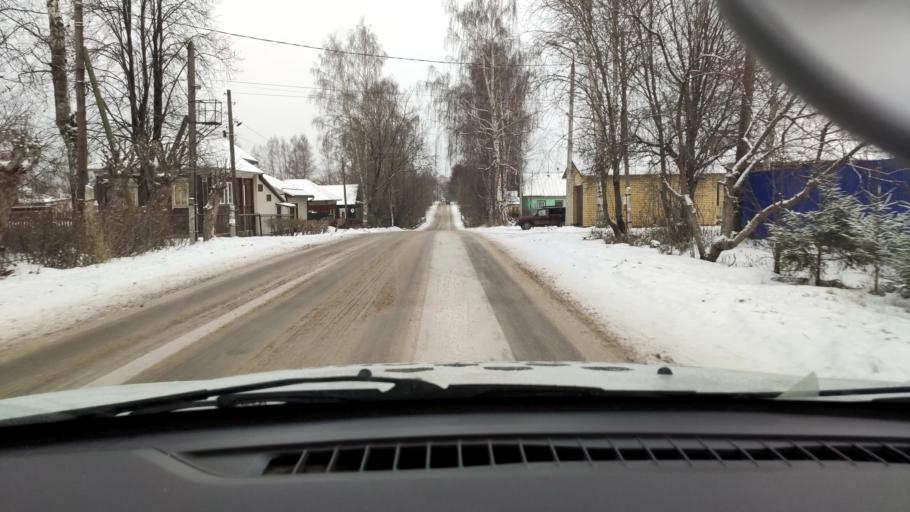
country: RU
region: Perm
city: Polazna
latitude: 58.1194
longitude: 56.3947
